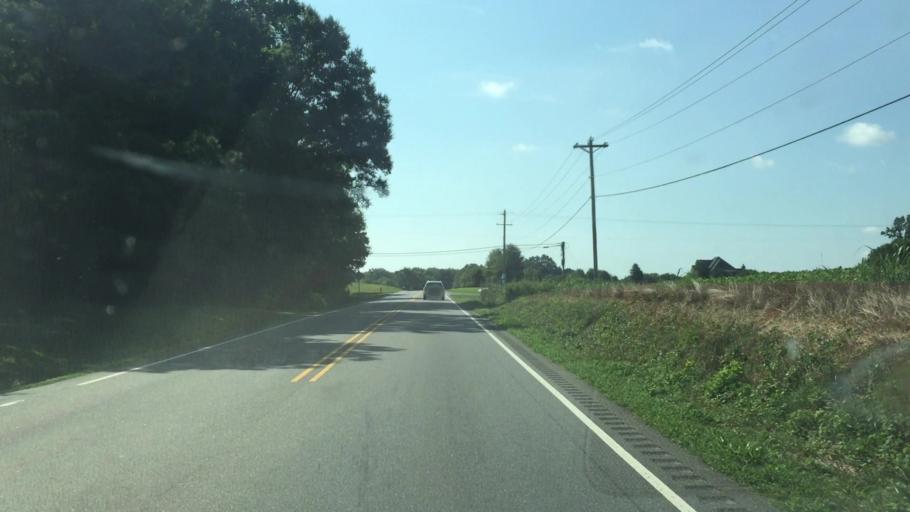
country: US
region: North Carolina
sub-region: Union County
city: Fairview
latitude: 35.1429
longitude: -80.5478
